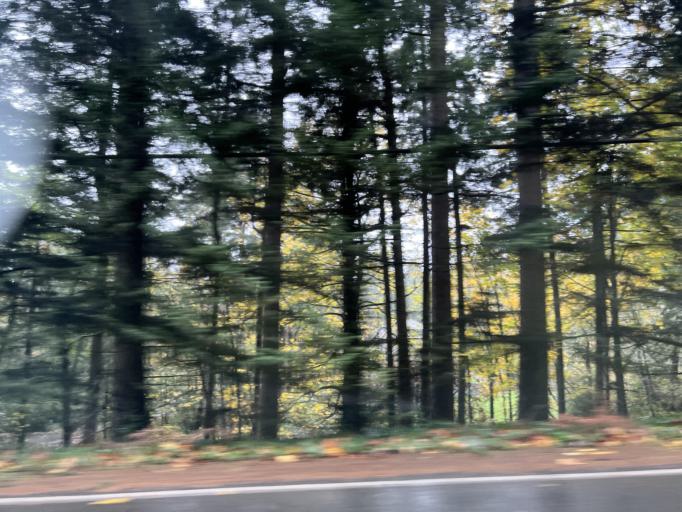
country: US
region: Washington
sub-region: Kitsap County
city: Bainbridge Island
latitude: 47.6625
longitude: -122.5211
